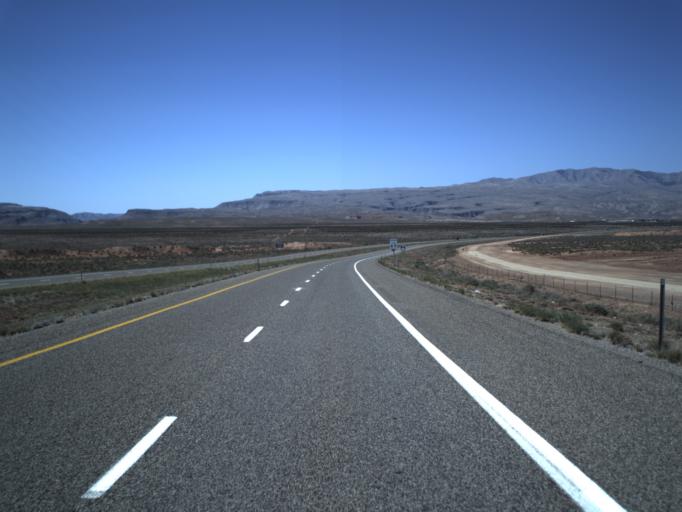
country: US
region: Utah
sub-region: Washington County
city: Saint George
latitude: 37.0008
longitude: -113.5684
